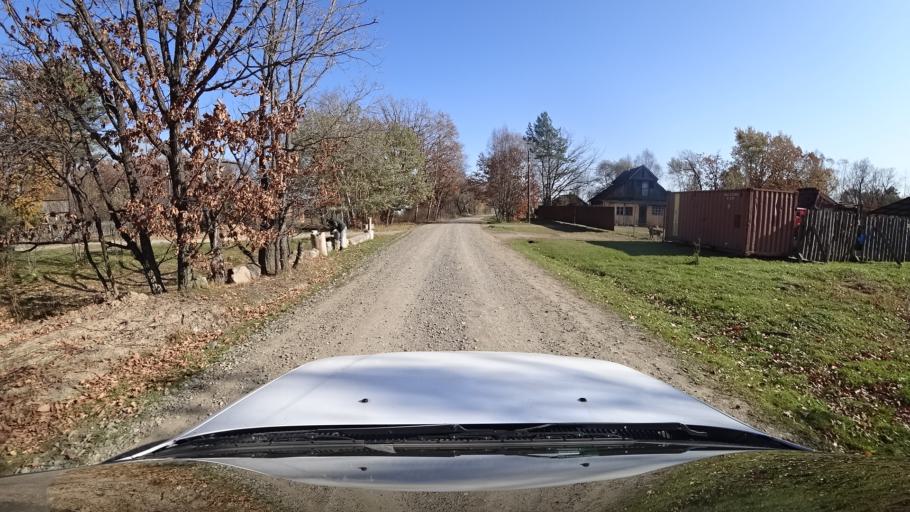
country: RU
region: Primorskiy
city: Dal'nerechensk
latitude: 45.8824
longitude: 133.7244
